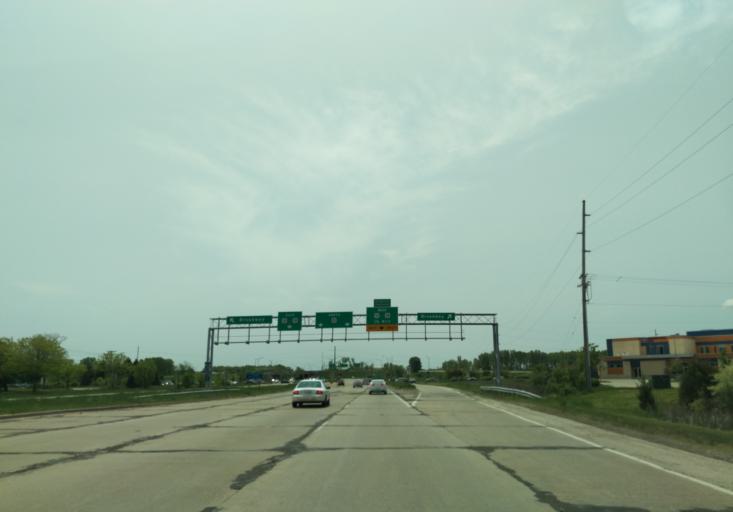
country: US
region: Wisconsin
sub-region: Dane County
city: Monona
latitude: 43.0505
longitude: -89.3083
